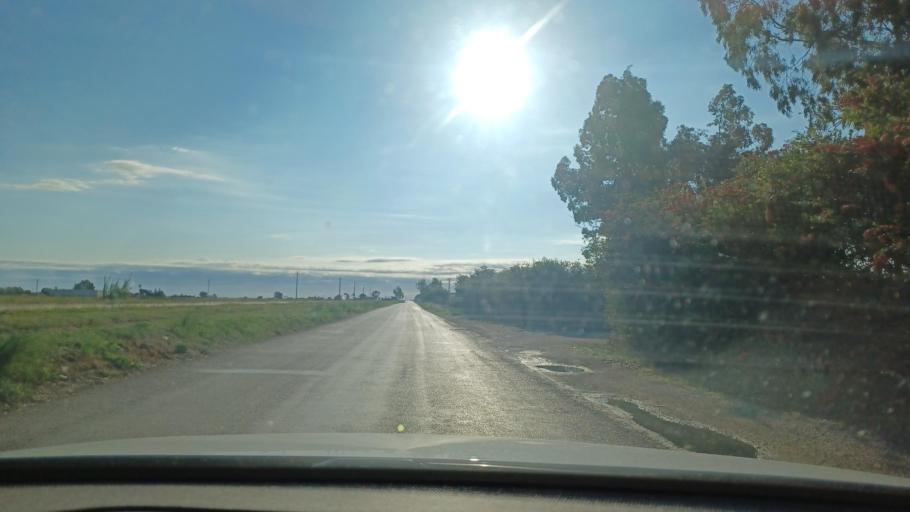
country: ES
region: Catalonia
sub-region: Provincia de Tarragona
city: Amposta
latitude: 40.7008
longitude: 0.6031
